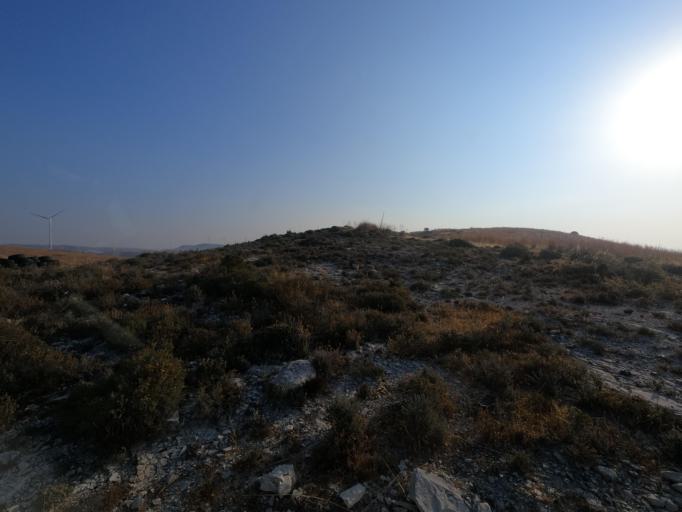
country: CY
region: Larnaka
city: Psevdas
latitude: 34.9177
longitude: 33.5007
